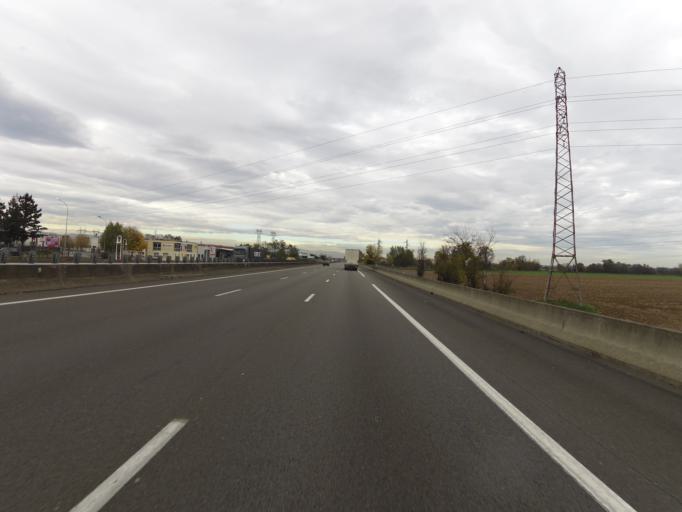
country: FR
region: Rhone-Alpes
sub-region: Departement du Rhone
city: Villefranche-sur-Saone
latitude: 46.0068
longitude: 4.7317
